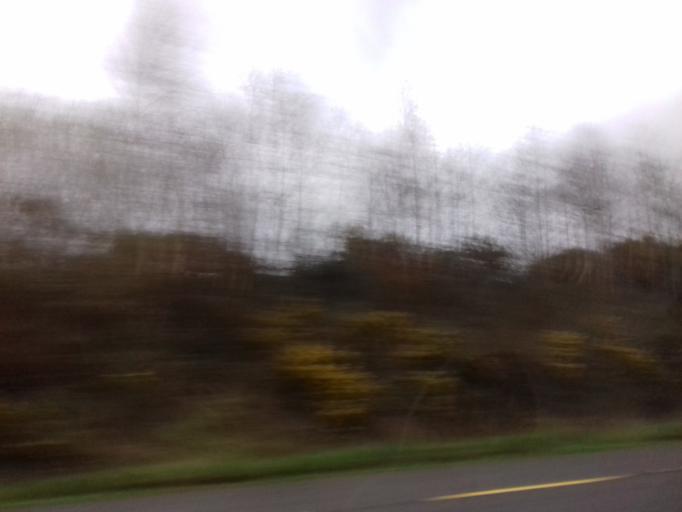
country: IE
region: Munster
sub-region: County Limerick
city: Abbeyfeale
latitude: 52.3423
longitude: -9.3461
